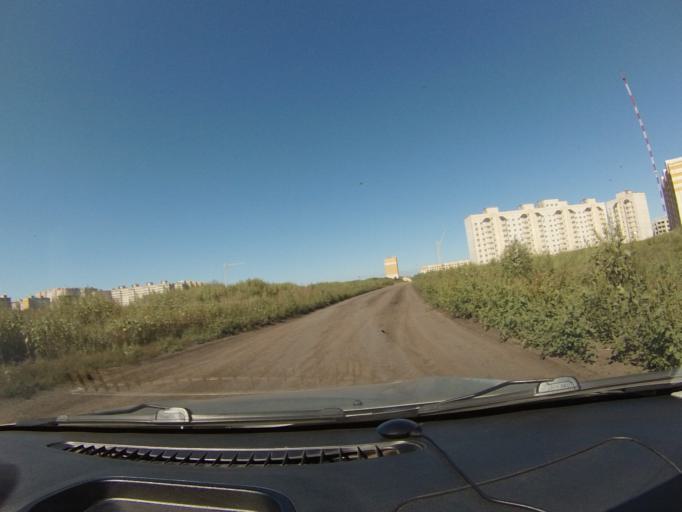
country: RU
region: Tambov
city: Tambov
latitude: 52.7743
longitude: 41.4104
